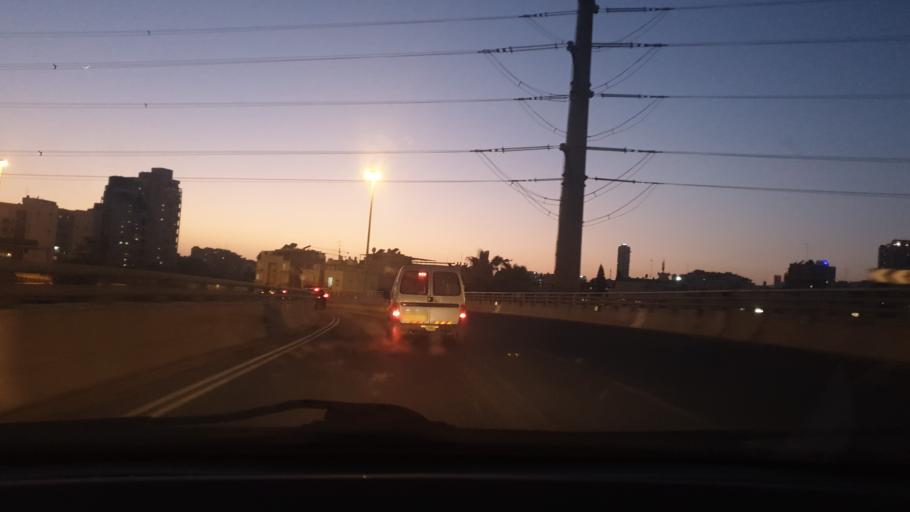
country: IL
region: Tel Aviv
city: Giv`at Shemu'el
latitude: 32.0653
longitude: 34.8388
